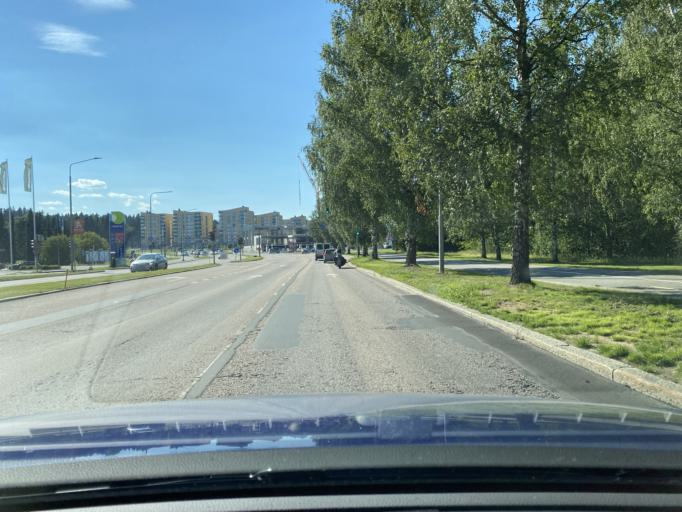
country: FI
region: Pirkanmaa
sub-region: Tampere
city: Tampere
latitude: 61.4936
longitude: 23.8256
